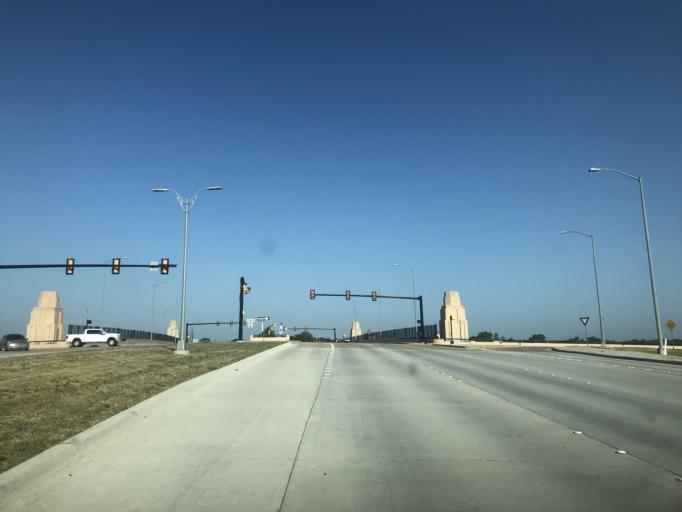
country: US
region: Texas
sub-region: Tarrant County
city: Benbrook
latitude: 32.6452
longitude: -97.4150
